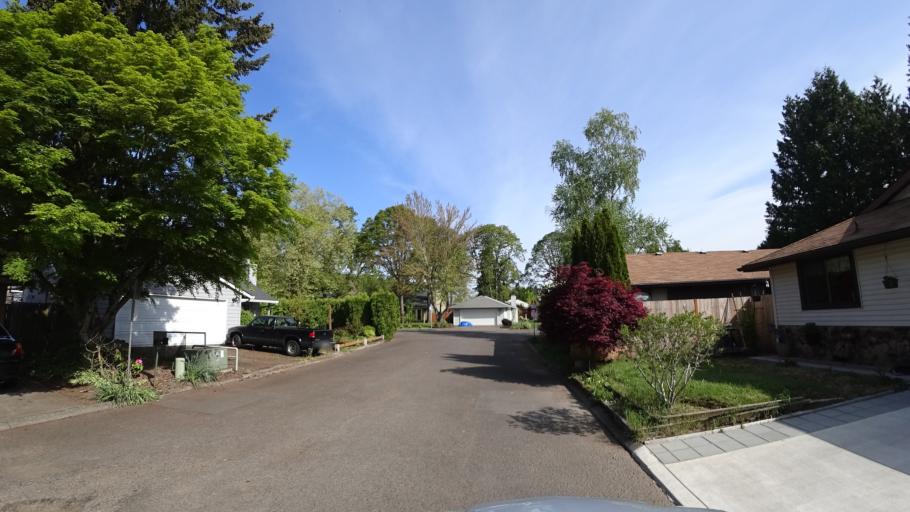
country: US
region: Oregon
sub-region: Washington County
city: Hillsboro
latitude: 45.5247
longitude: -122.9571
